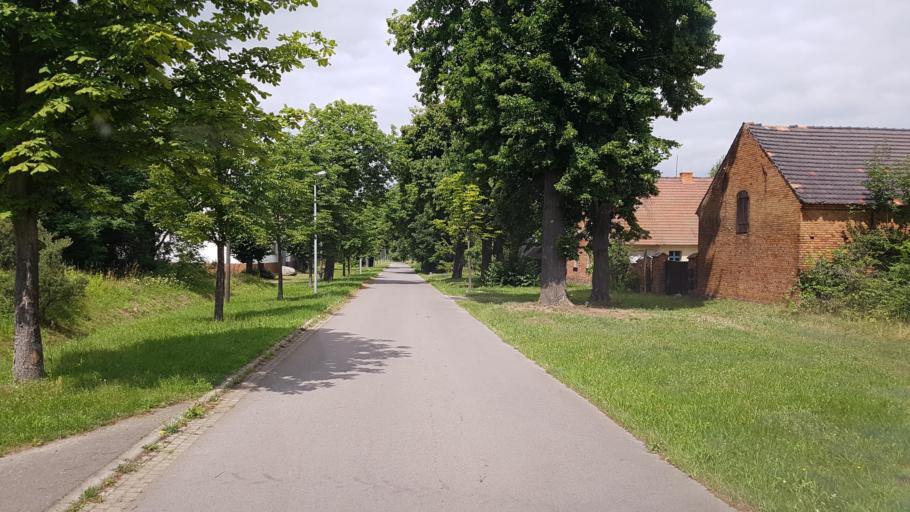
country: DE
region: Brandenburg
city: Altdobern
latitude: 51.6493
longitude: 14.0804
